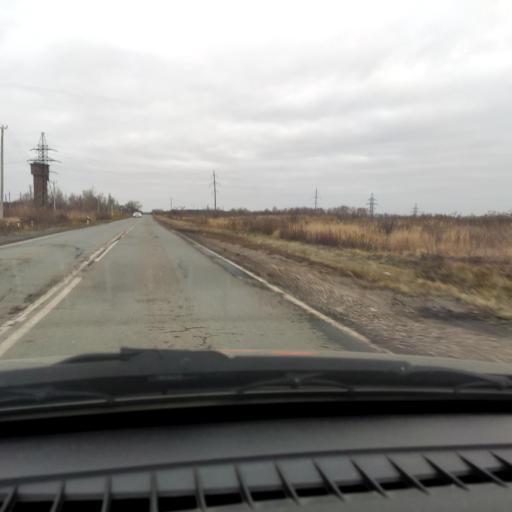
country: RU
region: Samara
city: Zhigulevsk
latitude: 53.3400
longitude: 49.4801
